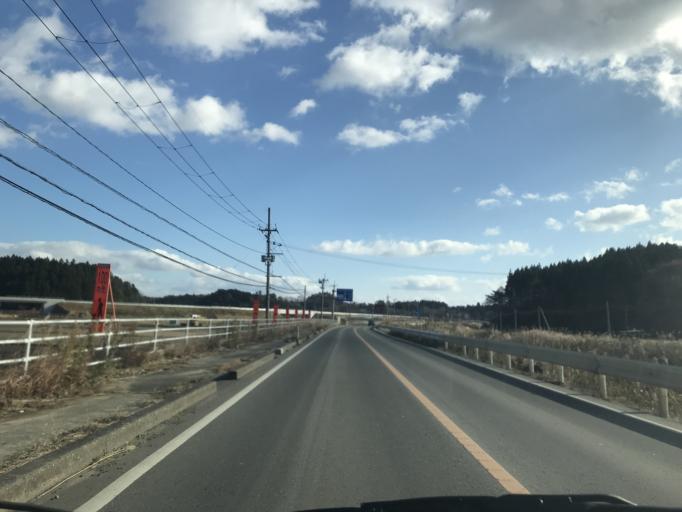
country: JP
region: Miyagi
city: Kogota
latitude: 38.7320
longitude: 141.0502
